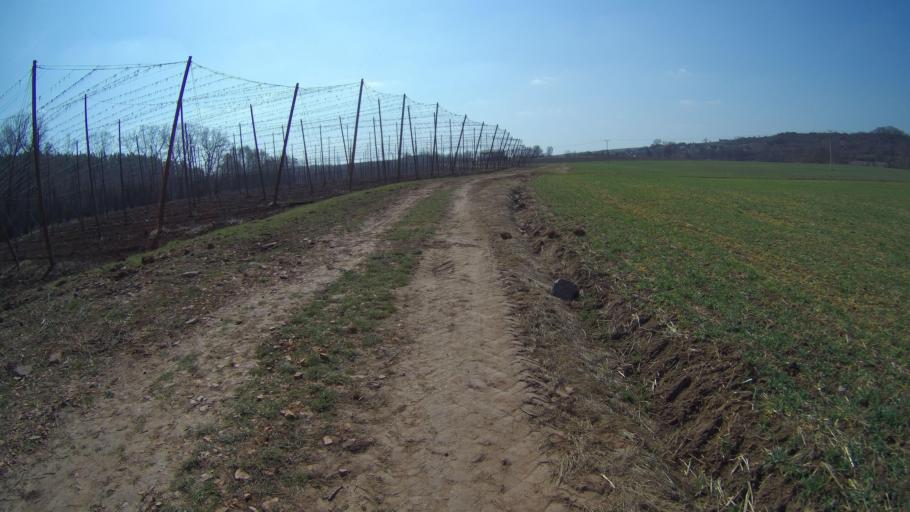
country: CZ
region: Ustecky
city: Zatec
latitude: 50.3000
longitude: 13.5859
